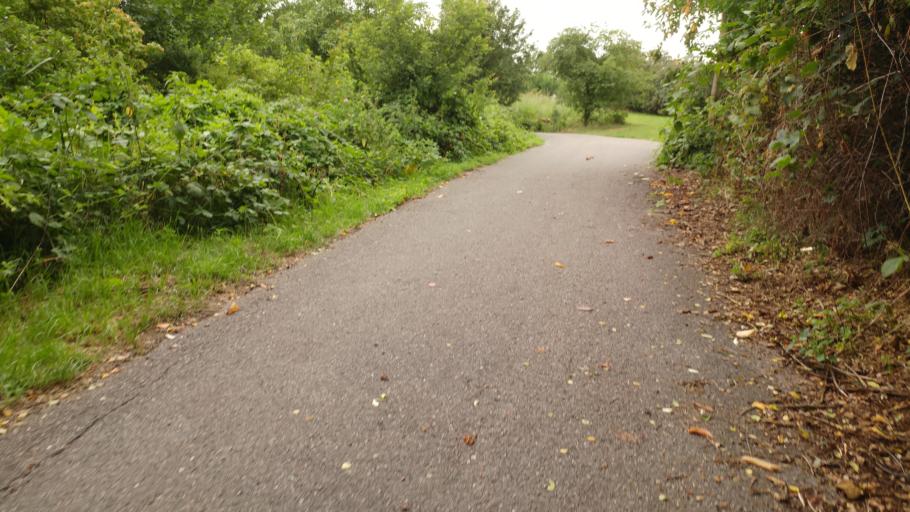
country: CZ
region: Central Bohemia
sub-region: Okres Praha-Zapad
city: Pruhonice
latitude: 50.0378
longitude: 14.5352
